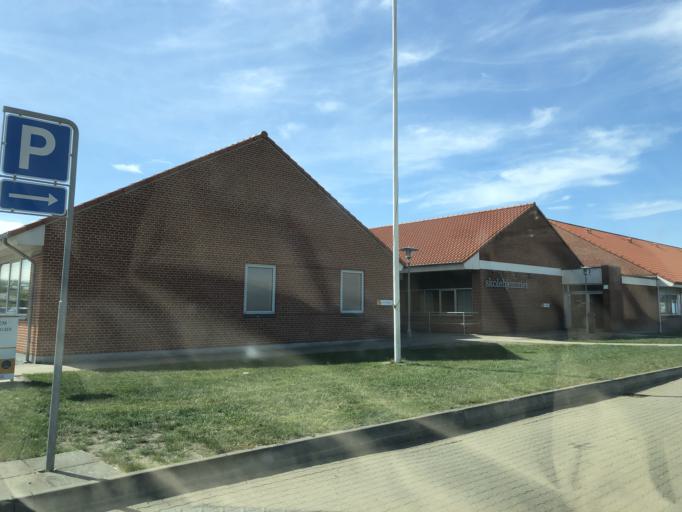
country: DK
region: Central Jutland
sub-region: Ringkobing-Skjern Kommune
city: Skjern
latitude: 55.9419
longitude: 8.5144
